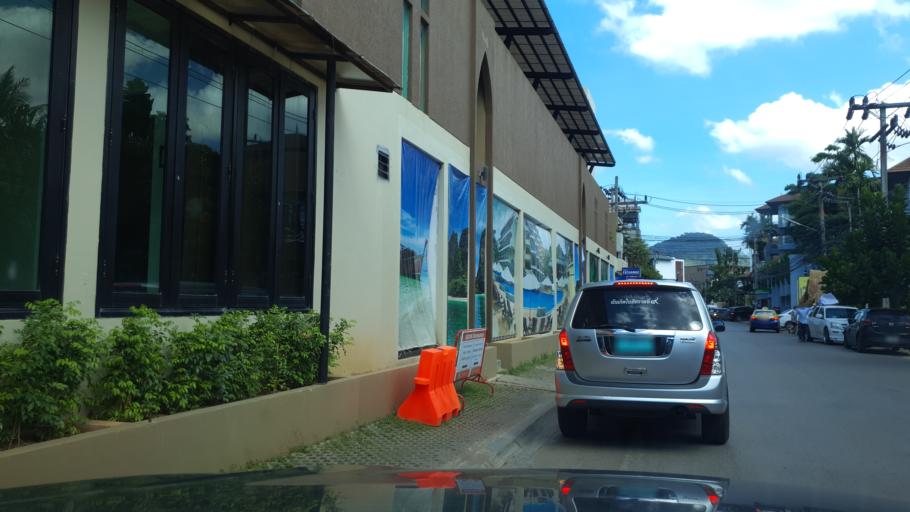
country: TH
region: Phangnga
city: Ban Ao Nang
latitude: 8.0387
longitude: 98.8173
